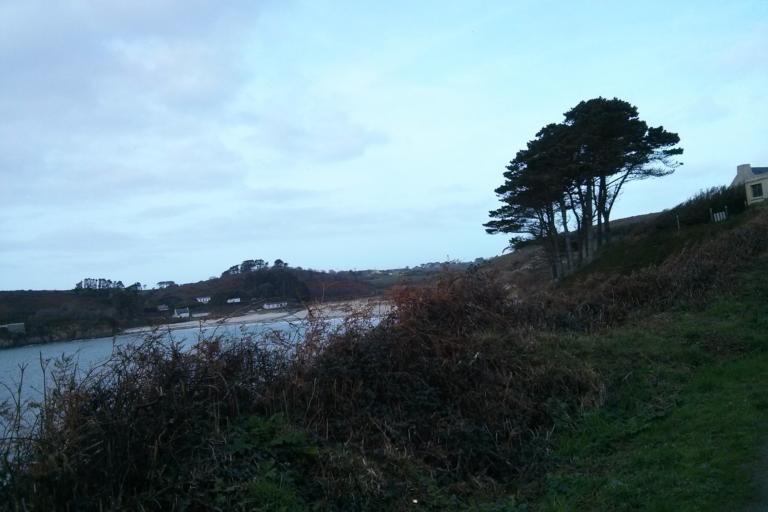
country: FR
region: Brittany
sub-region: Departement du Finistere
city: Le Conquet
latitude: 48.4027
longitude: -4.7735
